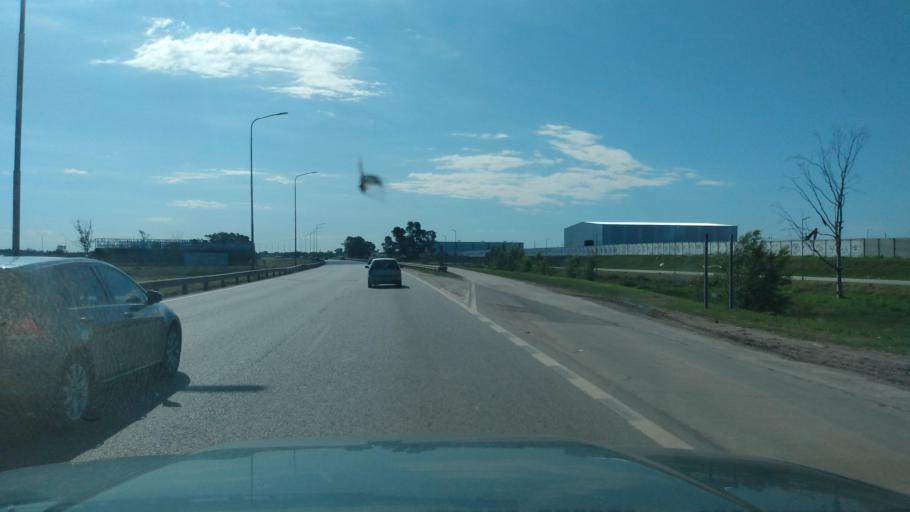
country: AR
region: Buenos Aires
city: Hurlingham
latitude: -34.5285
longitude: -58.5933
